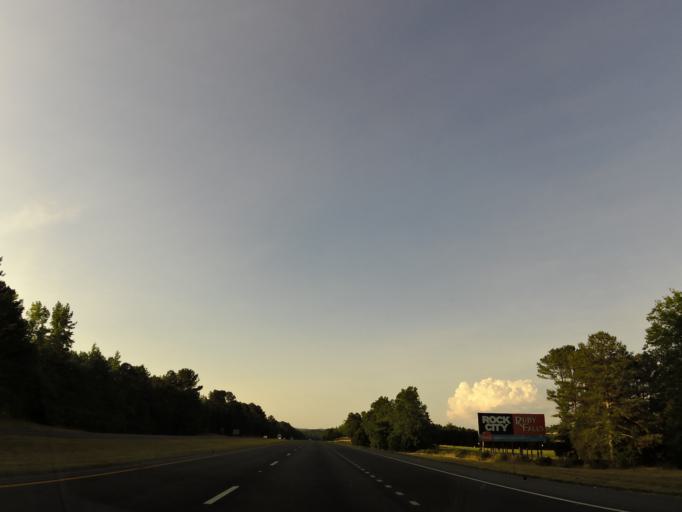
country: US
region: Alabama
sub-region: DeKalb County
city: Henagar
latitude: 34.5981
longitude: -85.6391
